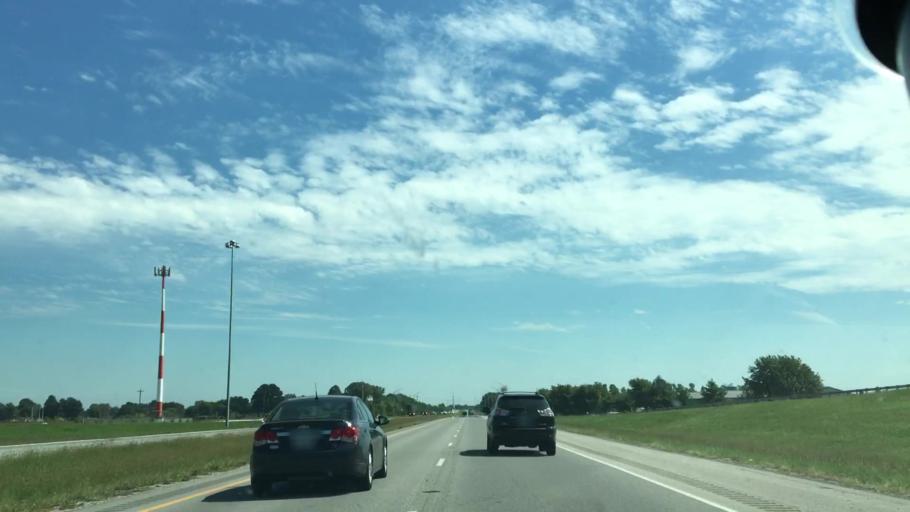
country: US
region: Kentucky
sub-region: Daviess County
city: Owensboro
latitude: 37.7425
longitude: -87.1490
